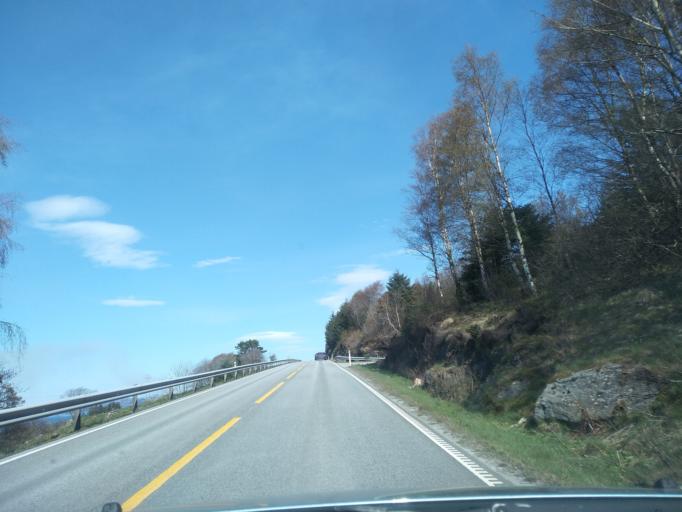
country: NO
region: Rogaland
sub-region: Bokn
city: Bokn
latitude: 59.2318
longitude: 5.4622
